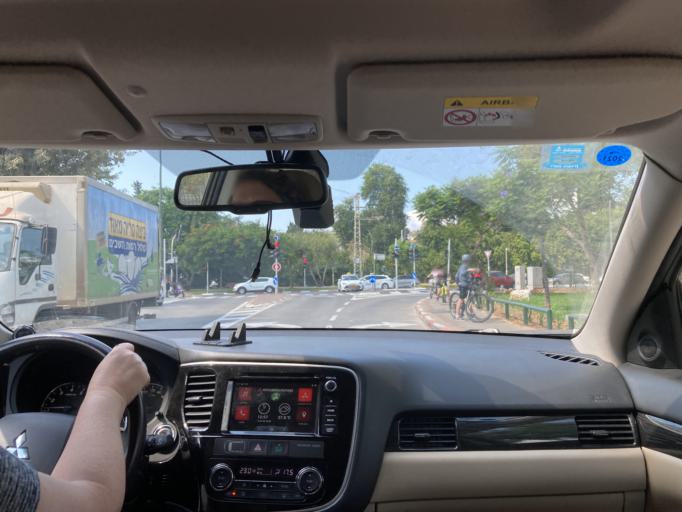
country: IL
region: Tel Aviv
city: Bene Beraq
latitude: 32.1121
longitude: 34.8398
